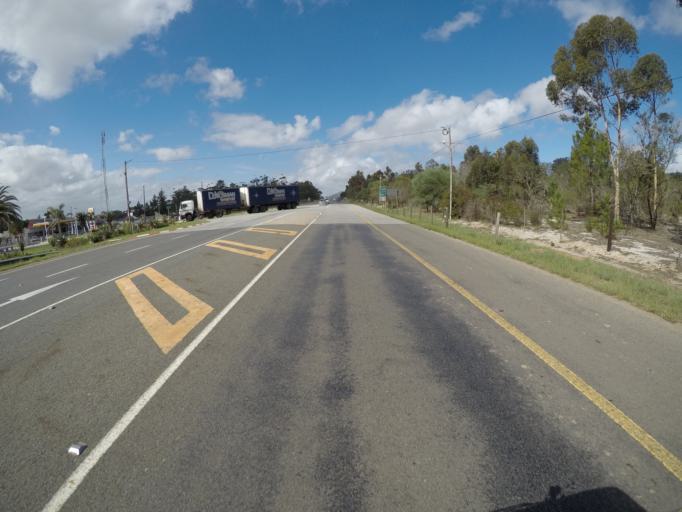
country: ZA
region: Western Cape
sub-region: Eden District Municipality
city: Riversdale
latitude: -34.2125
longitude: 21.5841
